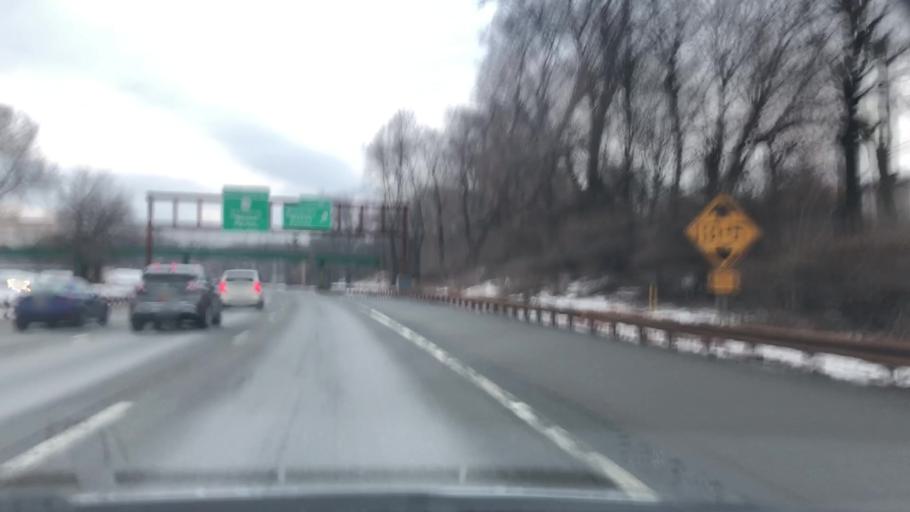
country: US
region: New Jersey
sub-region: Essex County
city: Brookdale
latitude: 40.8241
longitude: -74.1757
